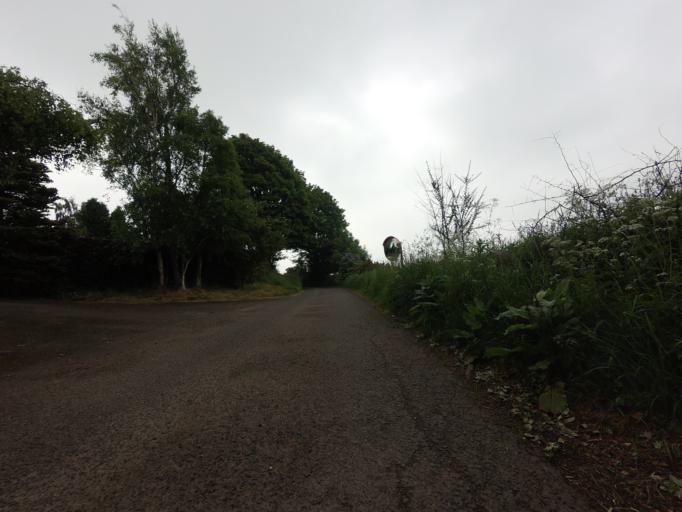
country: GB
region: Scotland
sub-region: Fife
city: Ballingry
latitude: 56.2304
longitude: -3.3432
